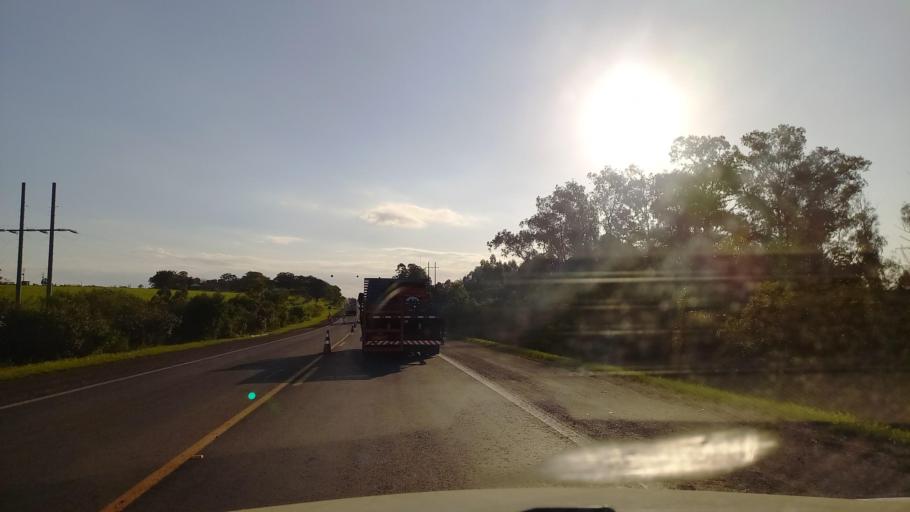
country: BR
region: Rio Grande do Sul
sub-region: Venancio Aires
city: Venancio Aires
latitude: -29.6433
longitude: -52.1320
